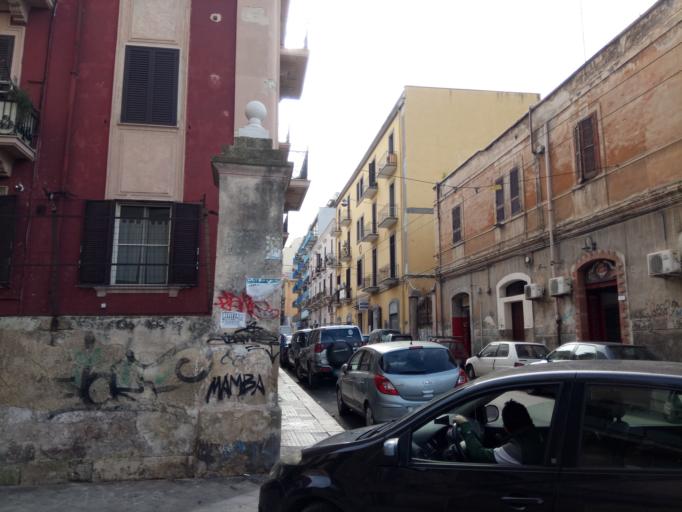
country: IT
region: Apulia
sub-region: Provincia di Bari
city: Bari
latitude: 41.1147
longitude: 16.8724
